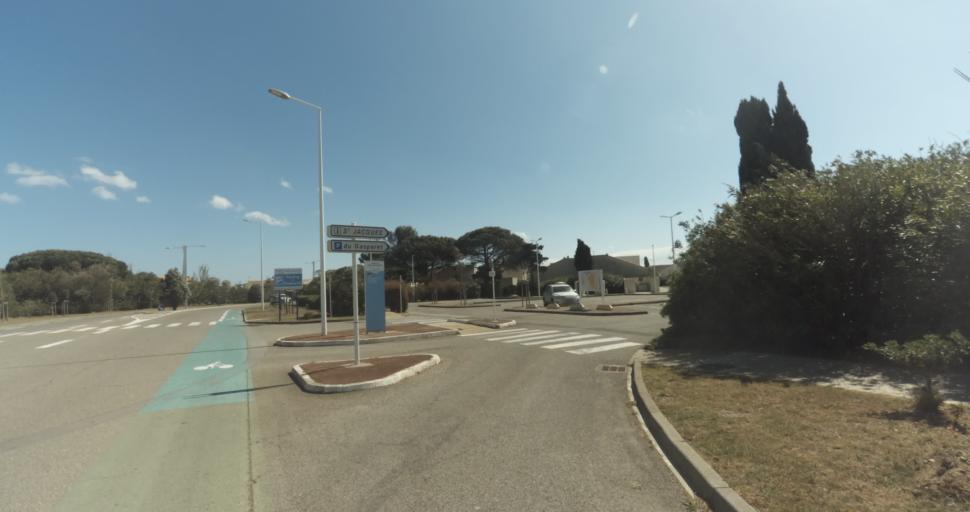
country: FR
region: Languedoc-Roussillon
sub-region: Departement de l'Aude
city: Leucate
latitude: 42.8555
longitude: 3.0400
